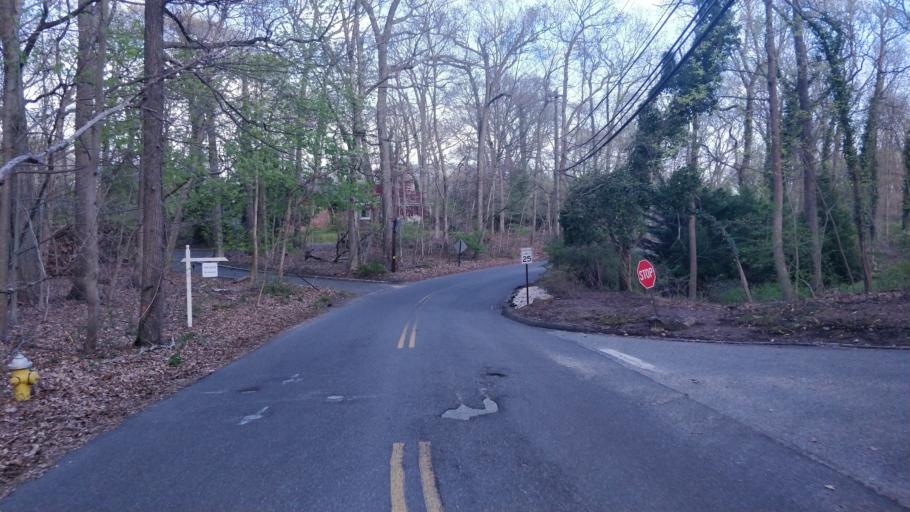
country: US
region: New York
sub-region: Suffolk County
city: Nissequogue
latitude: 40.8859
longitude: -73.1861
